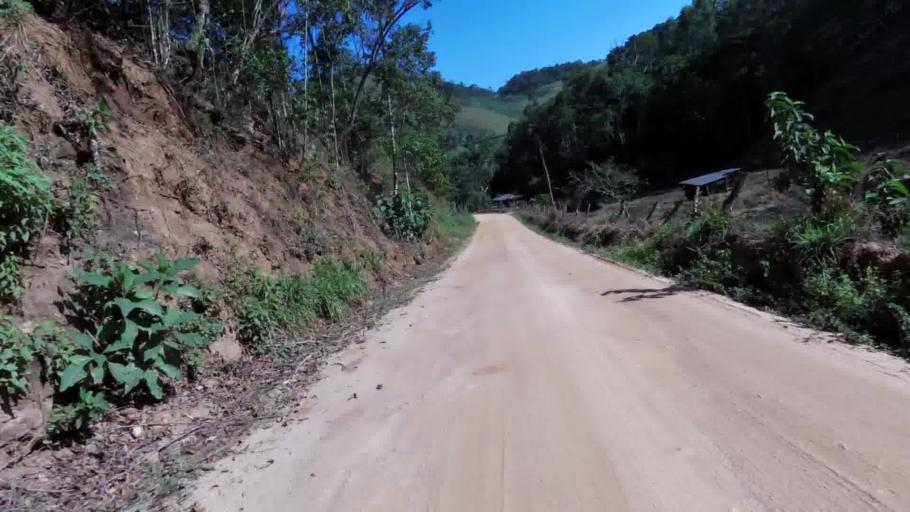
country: BR
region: Espirito Santo
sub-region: Alfredo Chaves
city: Alfredo Chaves
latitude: -20.5788
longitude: -40.7917
